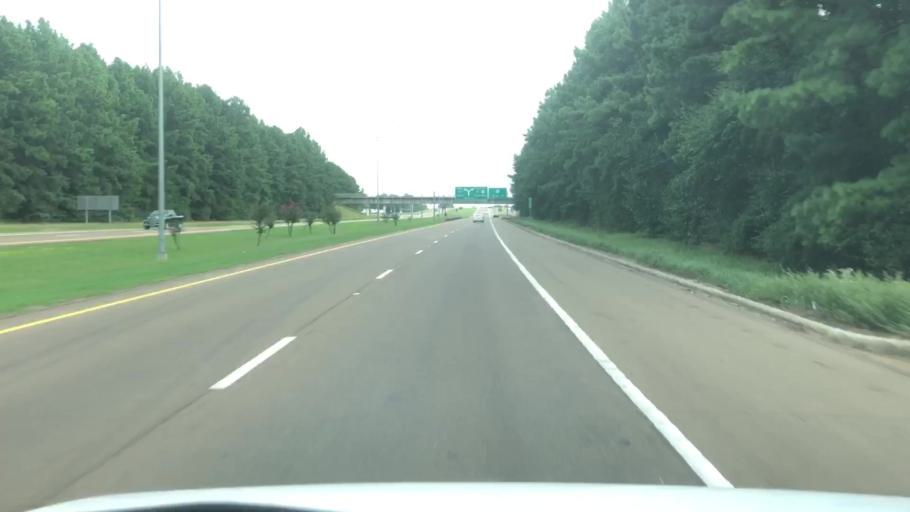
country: US
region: Texas
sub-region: Bowie County
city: Wake Village
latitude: 33.4120
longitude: -94.0971
